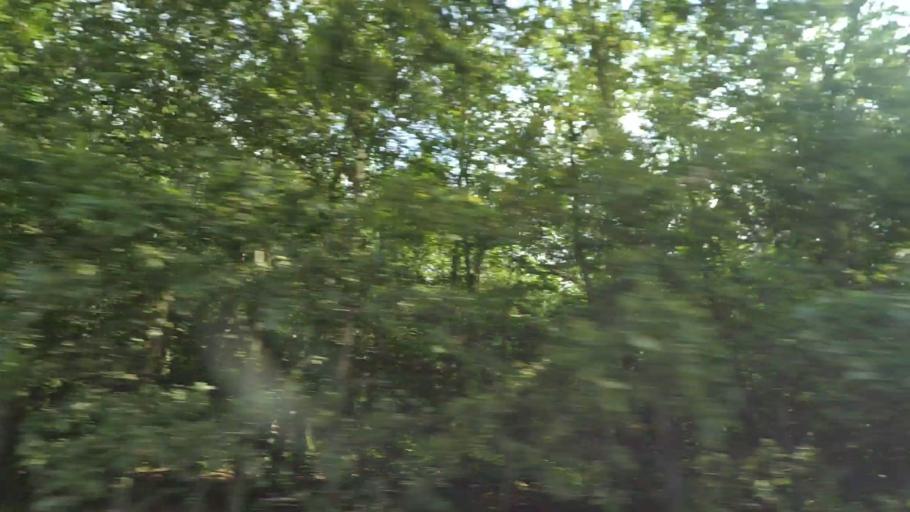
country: DK
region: Central Jutland
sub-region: Syddjurs Kommune
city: Ryomgard
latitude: 56.4587
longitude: 10.5405
